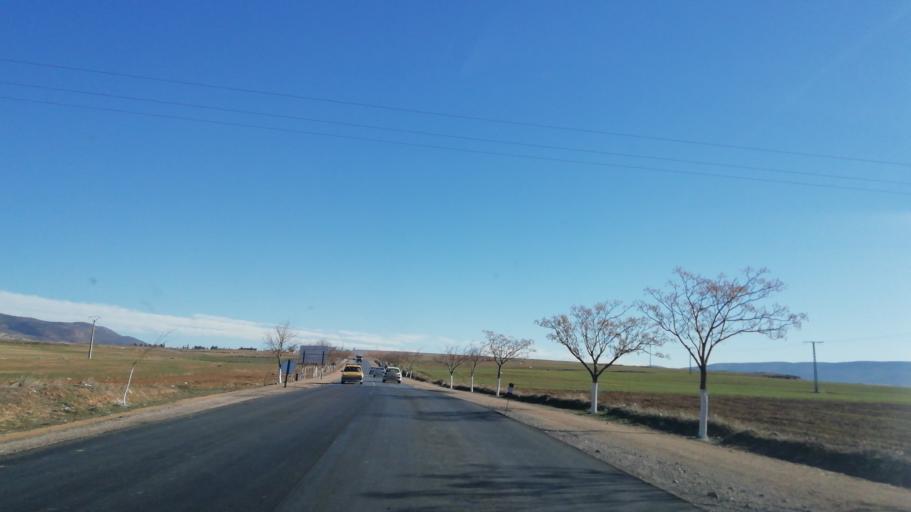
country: DZ
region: Tlemcen
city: Sebdou
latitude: 34.6560
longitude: -1.3049
